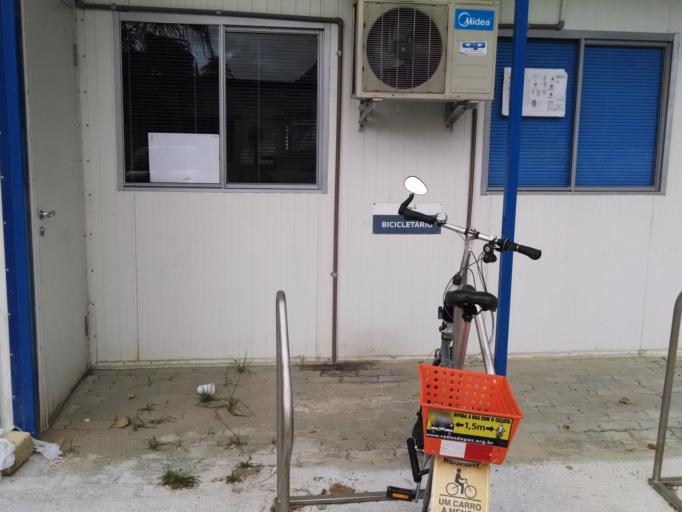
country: BR
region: Rio de Janeiro
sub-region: Rio De Janeiro
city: Rio de Janeiro
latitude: -22.9830
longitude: -43.2148
